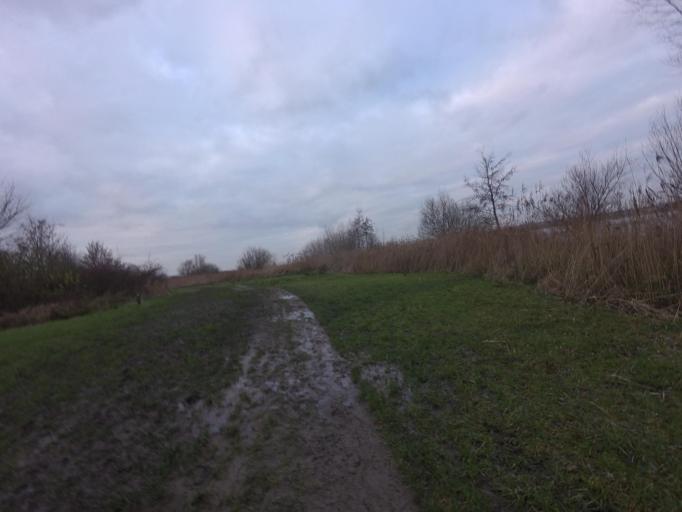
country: NL
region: Utrecht
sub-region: Stichtse Vecht
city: Spechtenkamp
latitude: 52.1145
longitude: 5.0213
